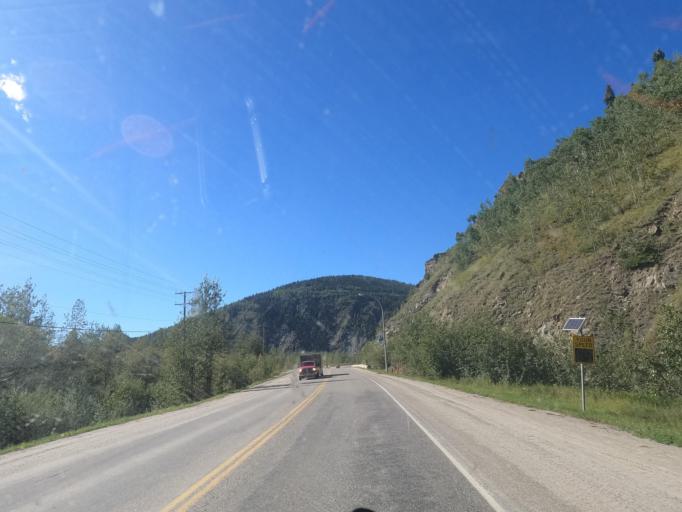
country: CA
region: Yukon
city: Dawson City
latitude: 64.0515
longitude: -139.4309
